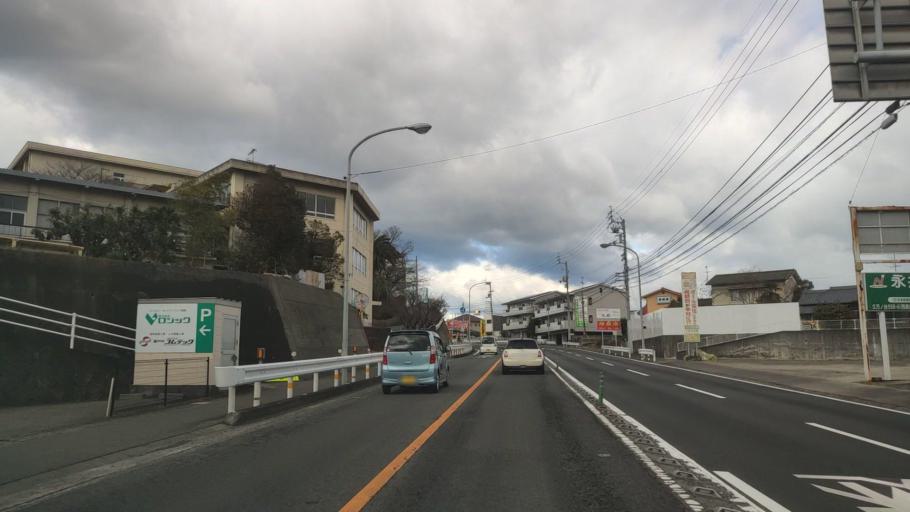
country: JP
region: Ehime
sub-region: Shikoku-chuo Shi
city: Matsuyama
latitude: 33.8562
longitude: 132.7424
